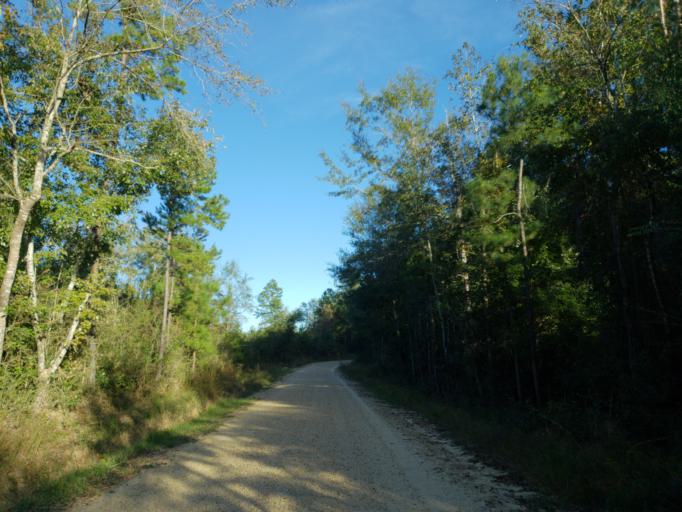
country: US
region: Mississippi
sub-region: Perry County
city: Richton
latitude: 31.3539
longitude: -88.8112
